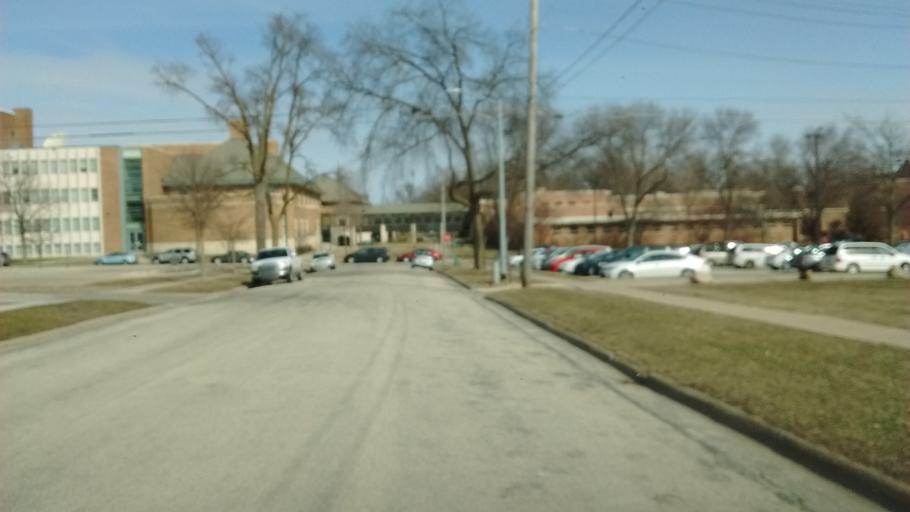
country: US
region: Iowa
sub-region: Bremer County
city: Waverly
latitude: 42.7259
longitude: -92.4831
